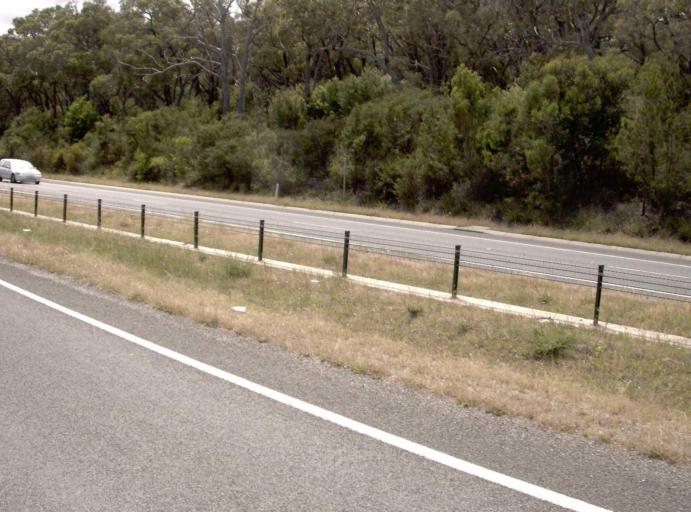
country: AU
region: Victoria
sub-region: Cardinia
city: Koo-Wee-Rup
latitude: -38.3878
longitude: 145.5461
